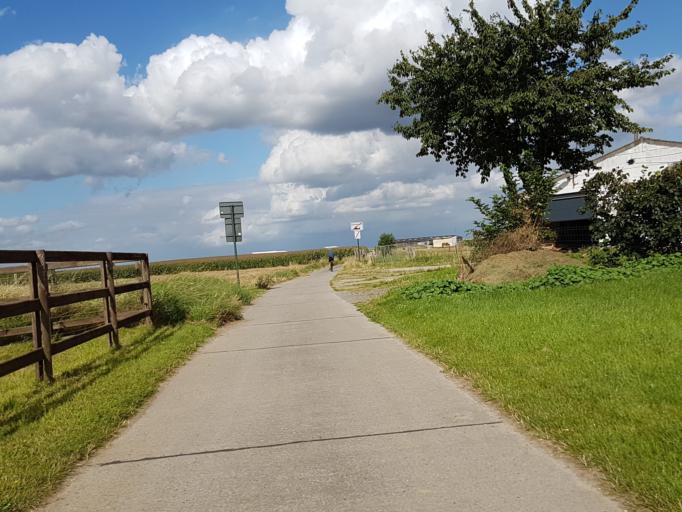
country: BE
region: Flanders
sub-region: Provincie Vlaams-Brabant
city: Steenokkerzeel
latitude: 50.9040
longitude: 4.5242
